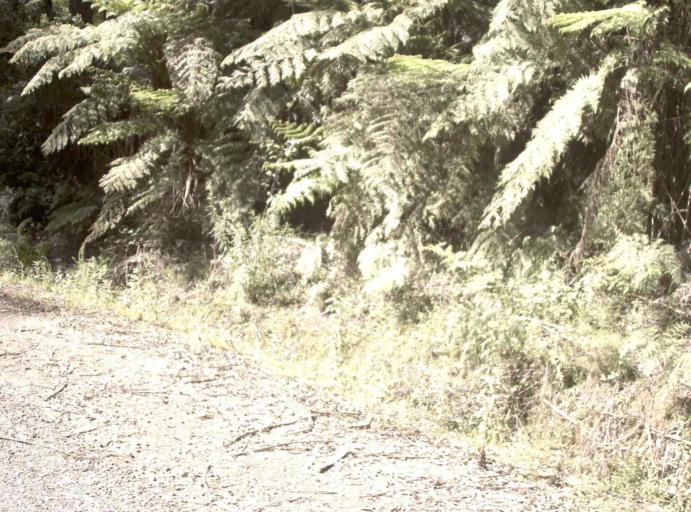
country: AU
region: New South Wales
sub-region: Bombala
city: Bombala
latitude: -37.2511
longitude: 148.7516
